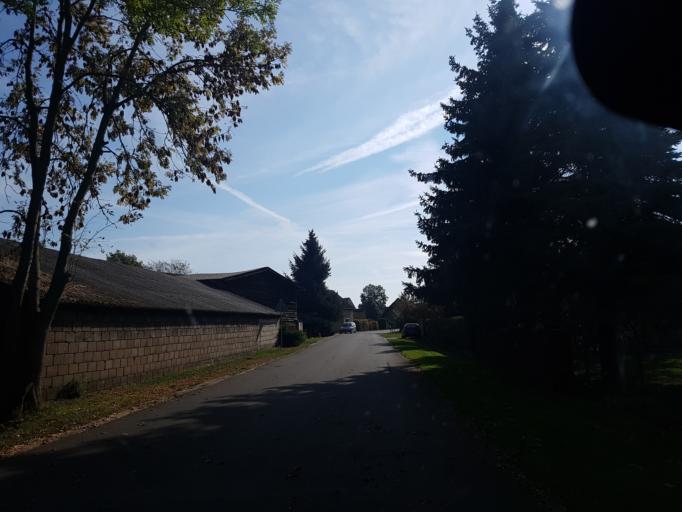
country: DE
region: Brandenburg
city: Ihlow
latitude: 51.8336
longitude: 13.3424
